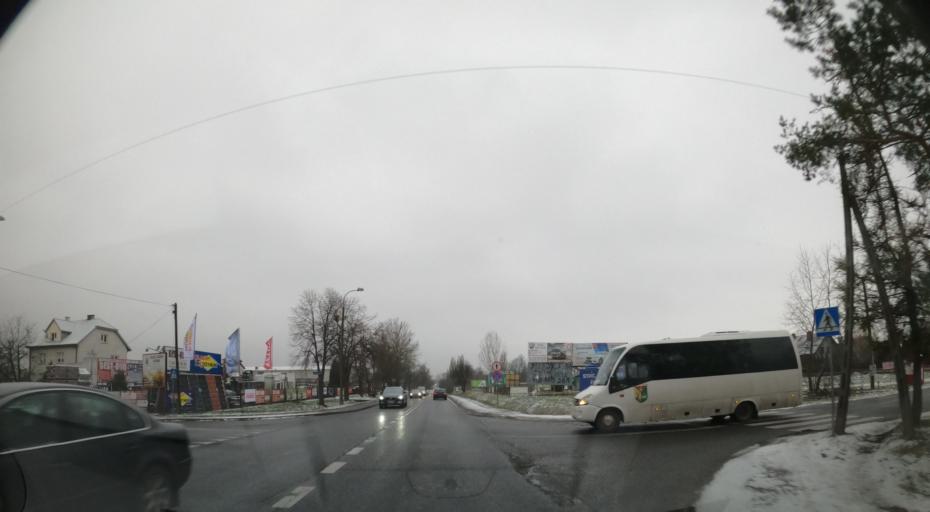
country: PL
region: Masovian Voivodeship
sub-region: Plock
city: Plock
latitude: 52.5323
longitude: 19.7721
